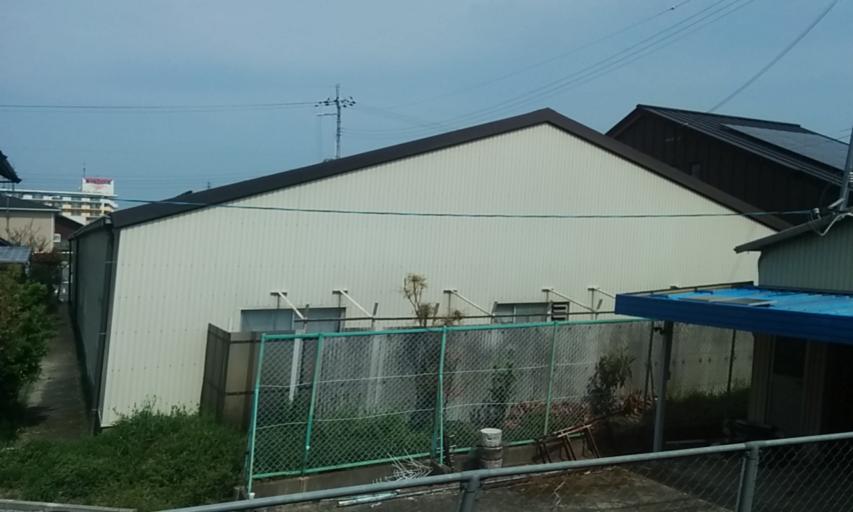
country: JP
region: Shiga Prefecture
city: Youkaichi
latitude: 35.1781
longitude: 136.1637
